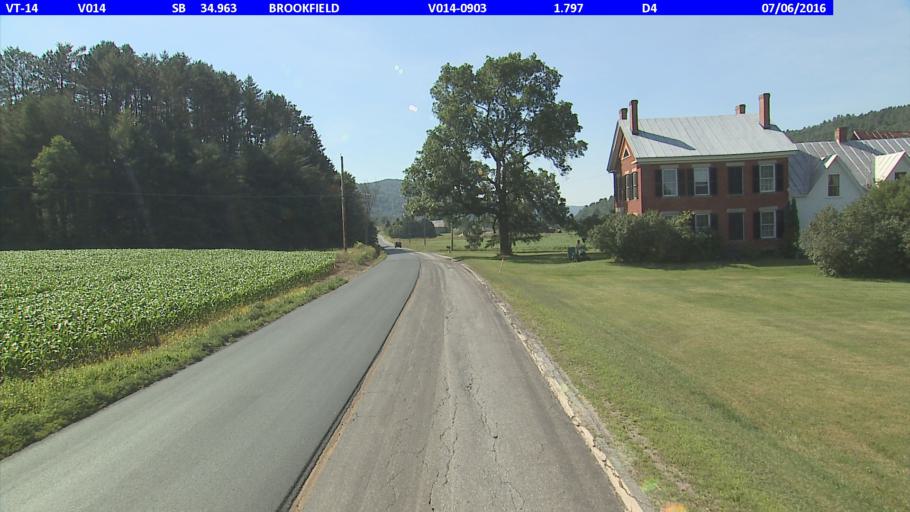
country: US
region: Vermont
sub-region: Orange County
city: Chelsea
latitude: 44.0037
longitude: -72.5638
